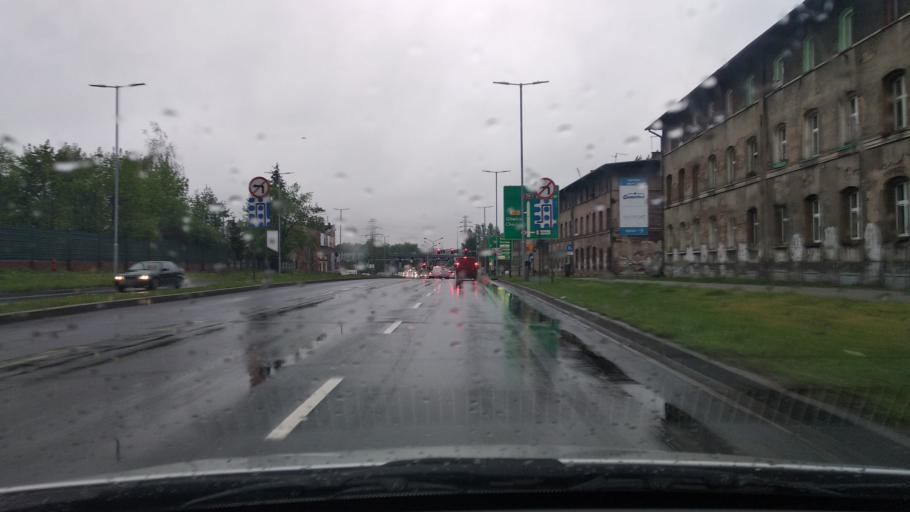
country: PL
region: Silesian Voivodeship
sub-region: Katowice
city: Katowice
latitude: 50.2659
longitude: 18.9889
